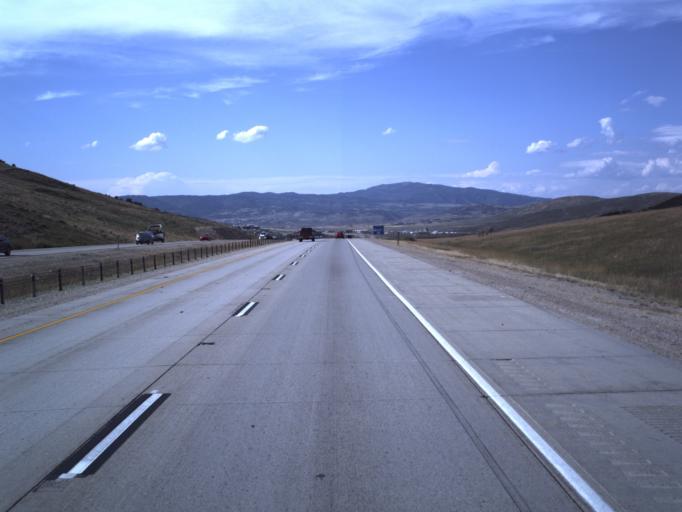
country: US
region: Utah
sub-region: Summit County
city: Park City
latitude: 40.6558
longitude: -111.4571
